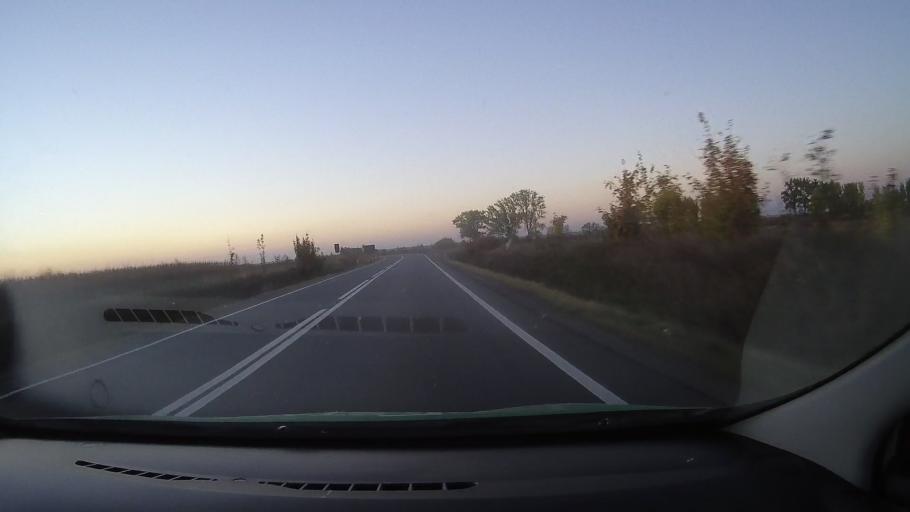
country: RO
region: Bihor
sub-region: Comuna Tarcea
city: Tarcea
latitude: 47.4330
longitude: 22.2051
